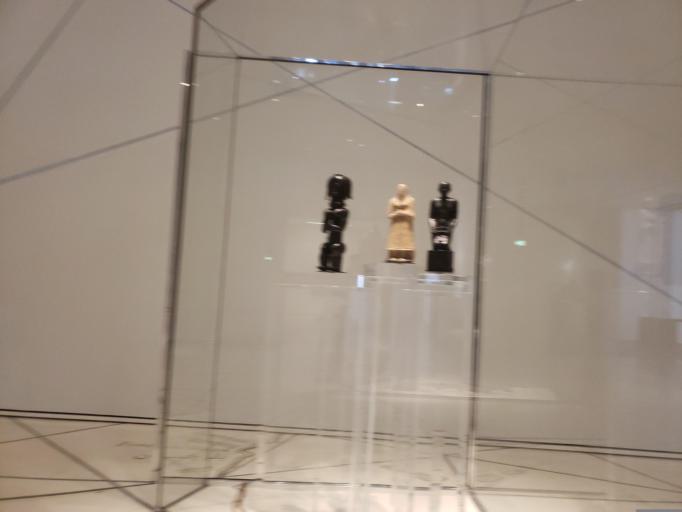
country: AE
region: Abu Dhabi
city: Abu Dhabi
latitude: 24.5336
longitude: 54.3990
